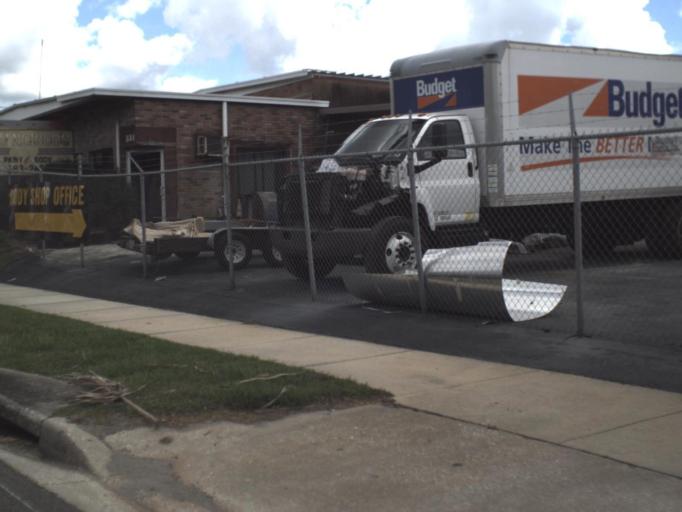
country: US
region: Florida
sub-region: Polk County
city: Winston
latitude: 28.0522
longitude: -81.9901
